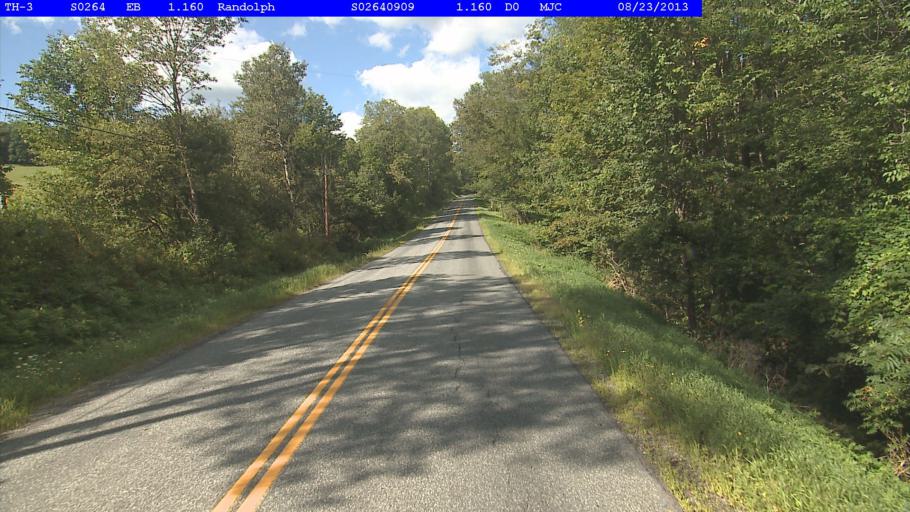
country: US
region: Vermont
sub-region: Orange County
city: Chelsea
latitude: 43.9452
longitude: -72.5388
